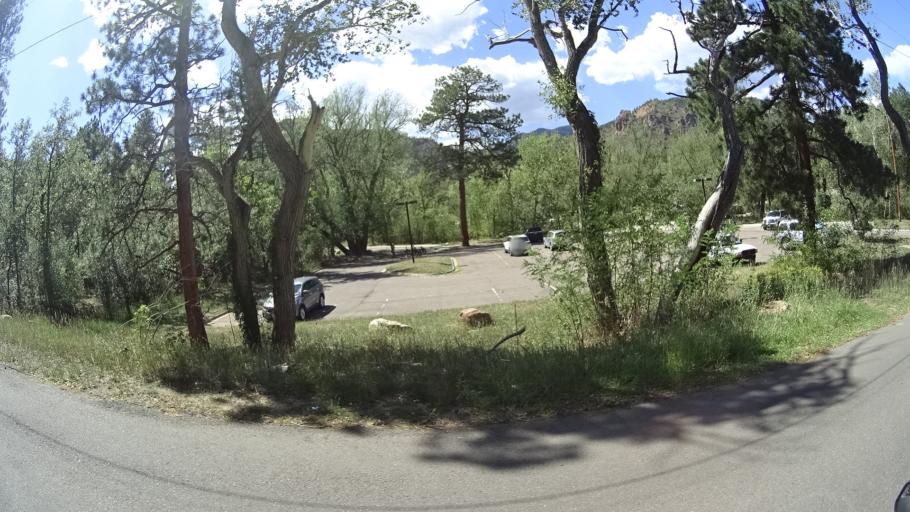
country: US
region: Colorado
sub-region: El Paso County
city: Colorado Springs
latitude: 38.7900
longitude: -104.8640
